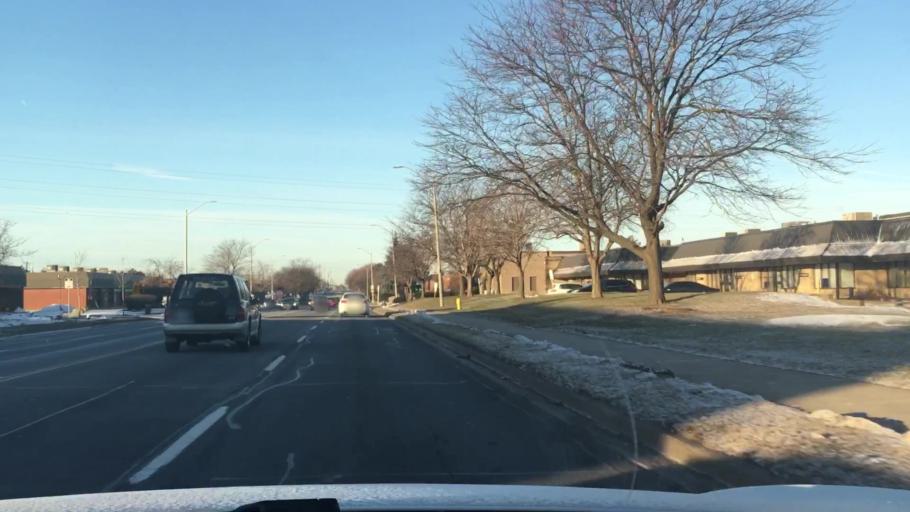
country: CA
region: Ontario
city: Markham
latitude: 43.8260
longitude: -79.3330
